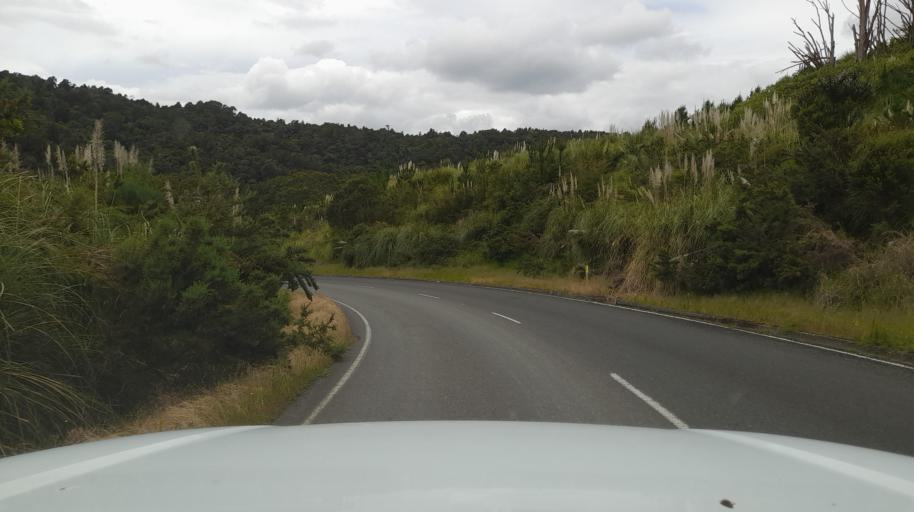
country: NZ
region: Northland
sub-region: Far North District
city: Kaitaia
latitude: -35.3577
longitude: 173.4631
